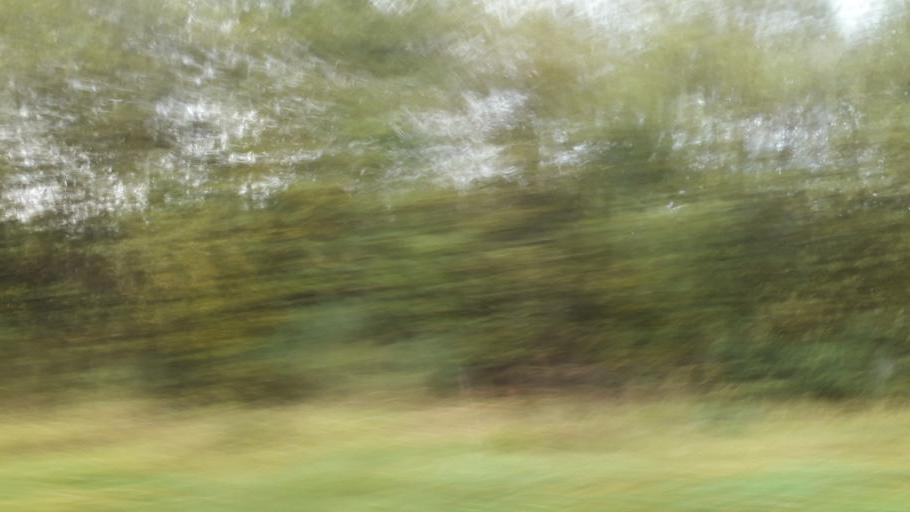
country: IE
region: Leinster
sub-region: An Longfort
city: Lanesborough
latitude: 53.7620
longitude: -8.0034
